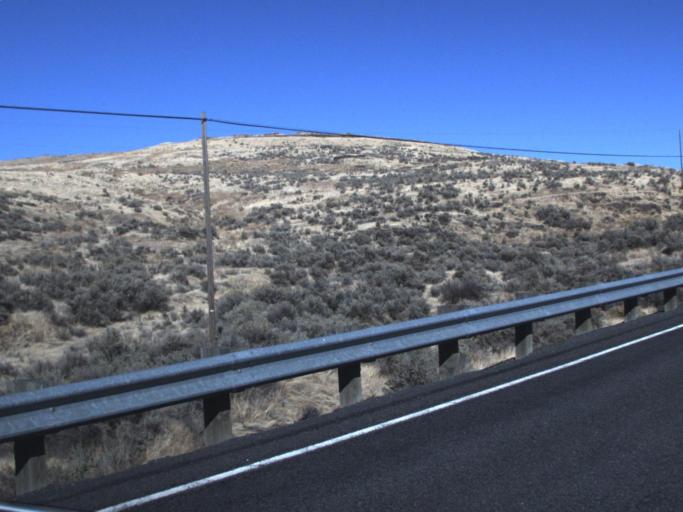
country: US
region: Washington
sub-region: Franklin County
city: Connell
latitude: 46.6472
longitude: -118.5382
